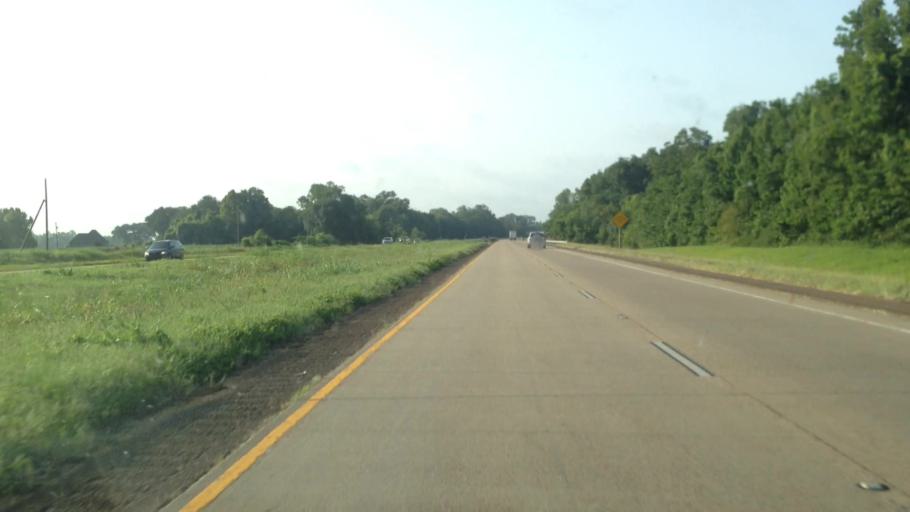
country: US
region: Louisiana
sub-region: Rapides Parish
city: Woodworth
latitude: 31.1355
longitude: -92.4482
